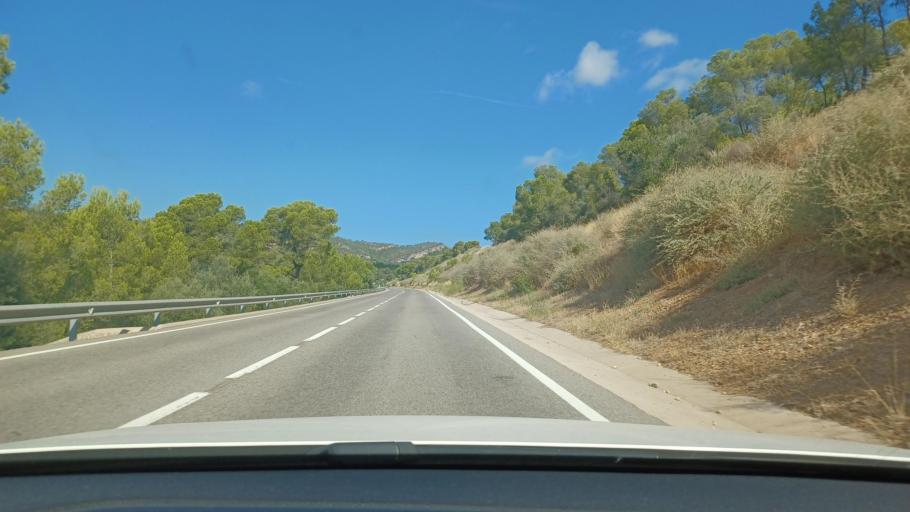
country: ES
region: Catalonia
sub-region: Provincia de Tarragona
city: Tivenys
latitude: 40.9352
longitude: 0.4729
